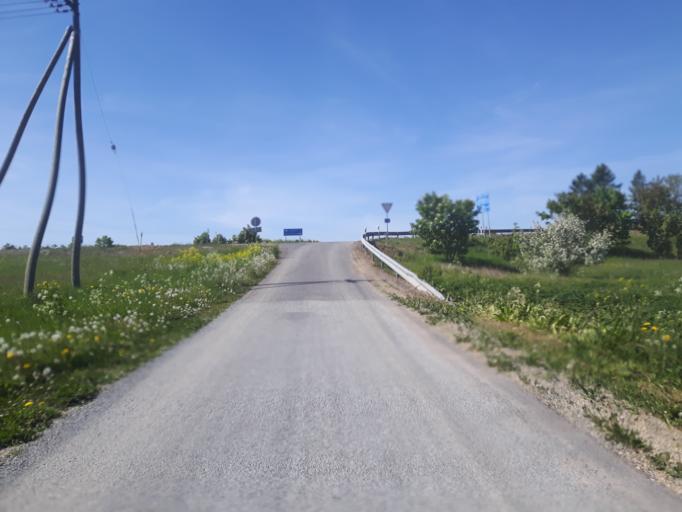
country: EE
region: Ida-Virumaa
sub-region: Kivioli linn
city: Kivioli
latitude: 59.4289
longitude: 26.9548
